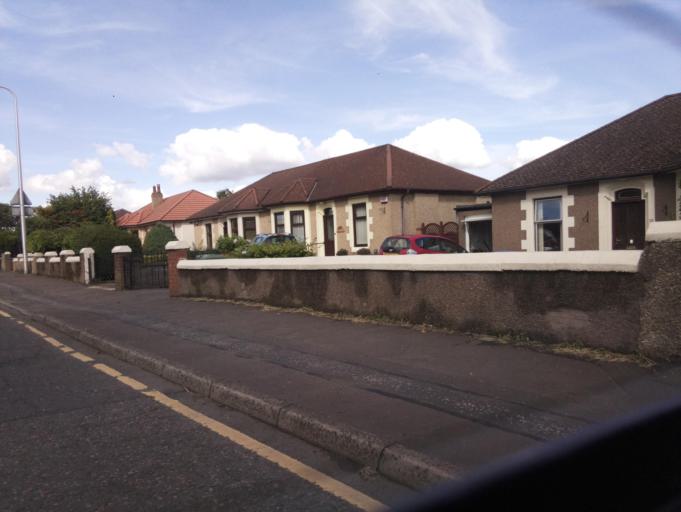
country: GB
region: Scotland
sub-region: Falkirk
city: Larbert
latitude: 56.0212
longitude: -3.8368
